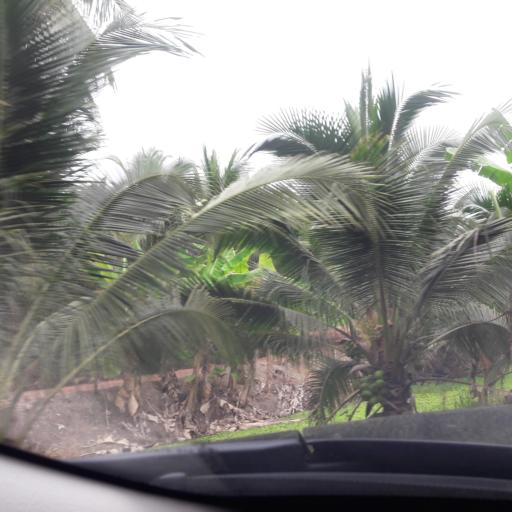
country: TH
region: Ratchaburi
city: Damnoen Saduak
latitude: 13.5786
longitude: 99.9462
